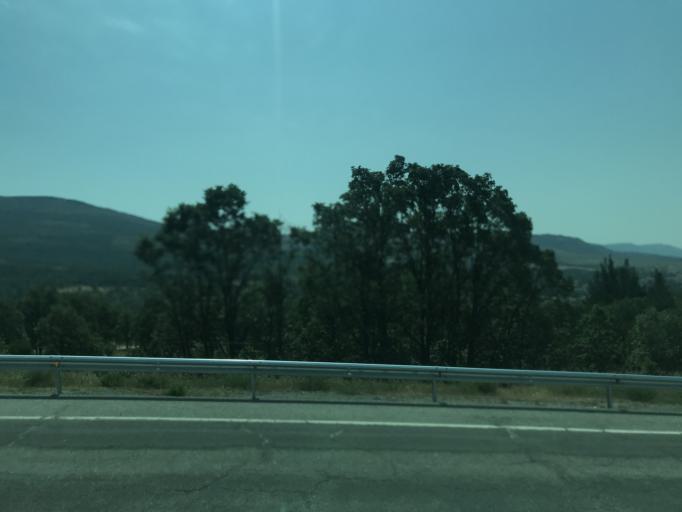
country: ES
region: Madrid
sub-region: Provincia de Madrid
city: Horcajo de la Sierra
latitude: 41.0823
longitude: -3.5978
